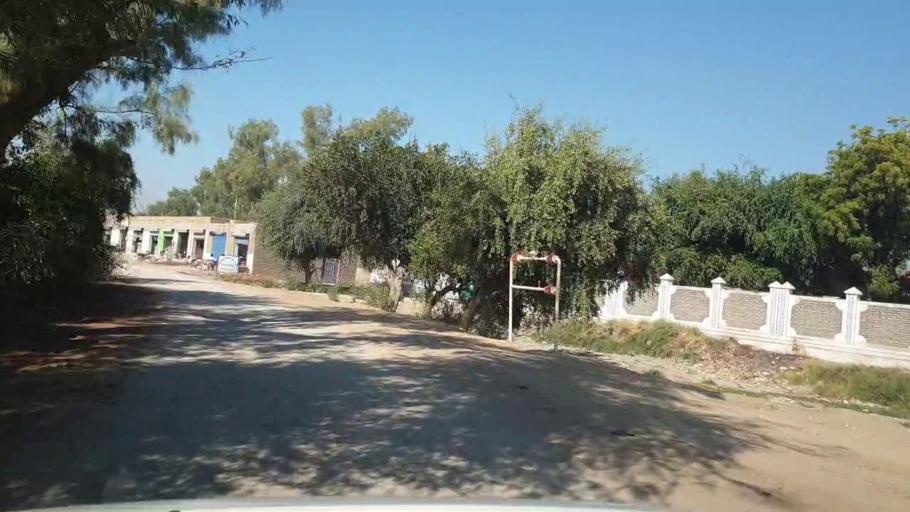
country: PK
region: Sindh
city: Bhan
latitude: 26.6490
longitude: 67.7139
